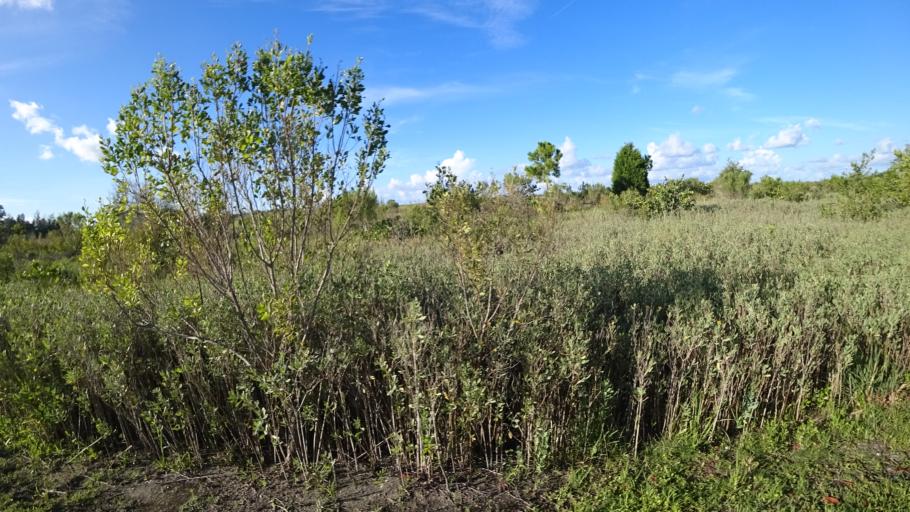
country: US
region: Florida
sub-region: Manatee County
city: Holmes Beach
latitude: 27.5128
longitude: -82.6678
